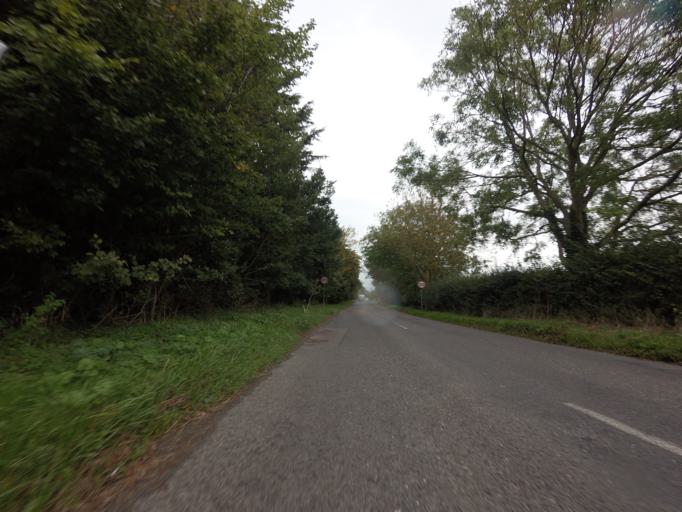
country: GB
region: England
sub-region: Cambridgeshire
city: Harston
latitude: 52.0858
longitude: 0.0757
